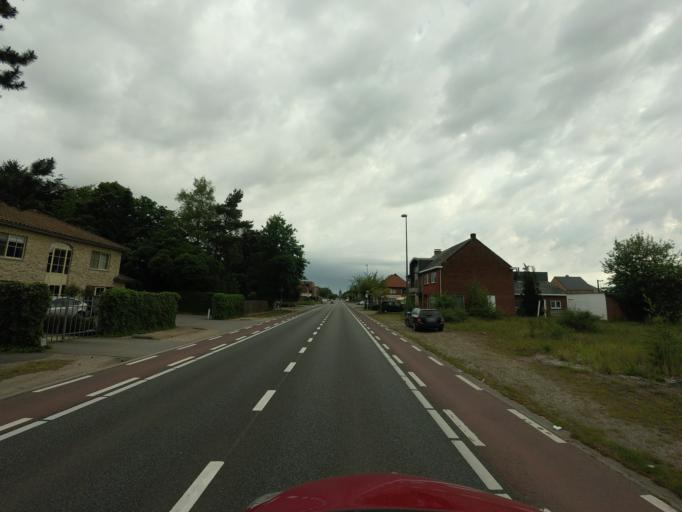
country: BE
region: Flanders
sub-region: Provincie Limburg
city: Lommel
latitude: 51.2159
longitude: 5.3132
